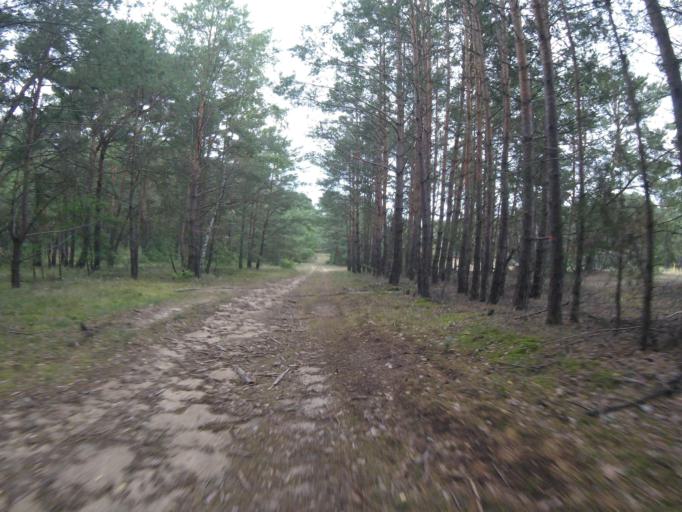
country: DE
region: Brandenburg
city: Bestensee
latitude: 52.2230
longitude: 13.6747
